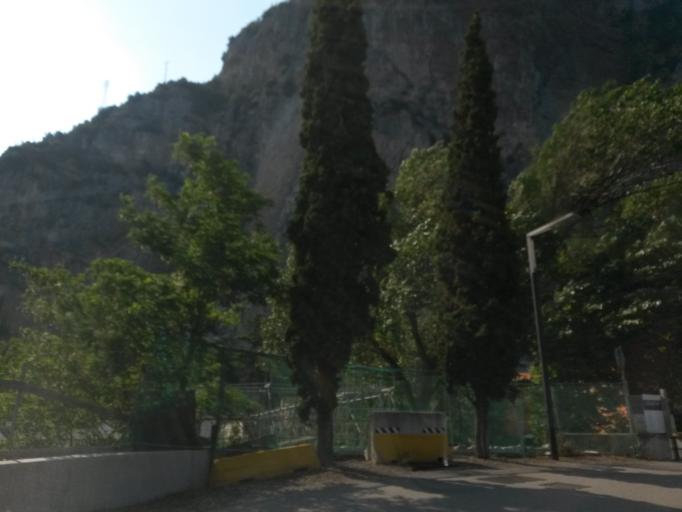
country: IT
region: Lombardy
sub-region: Provincia di Brescia
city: Pieve
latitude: 45.7540
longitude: 10.7507
